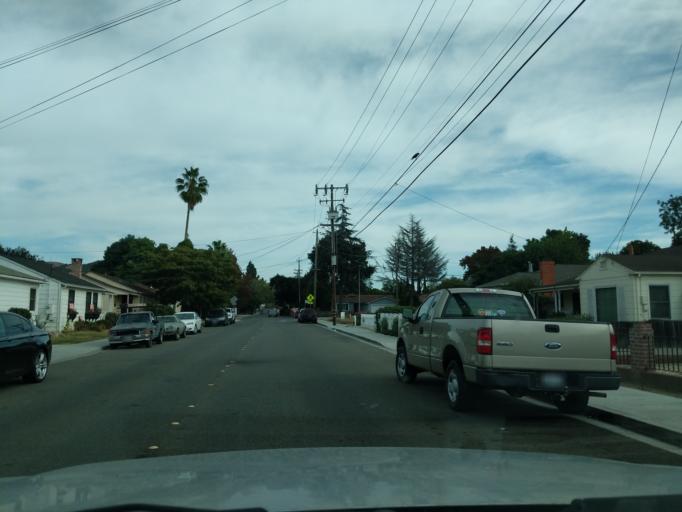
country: US
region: California
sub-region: Alameda County
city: Fremont
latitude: 37.5783
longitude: -121.9850
